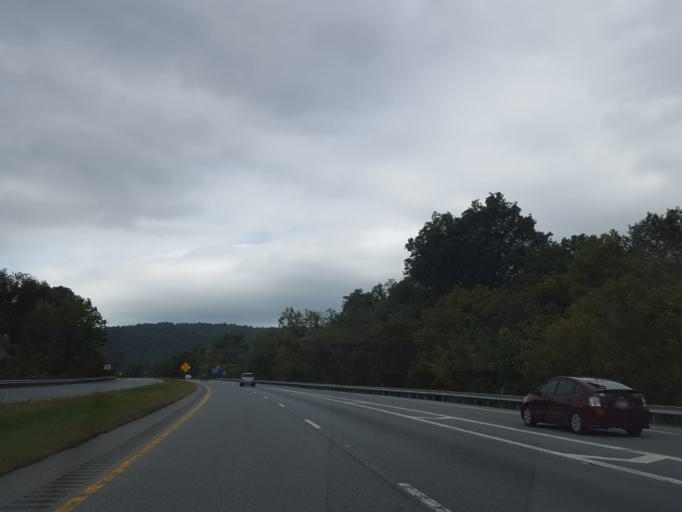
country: US
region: West Virginia
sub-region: Jefferson County
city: Bolivar
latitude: 39.3334
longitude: -77.6916
